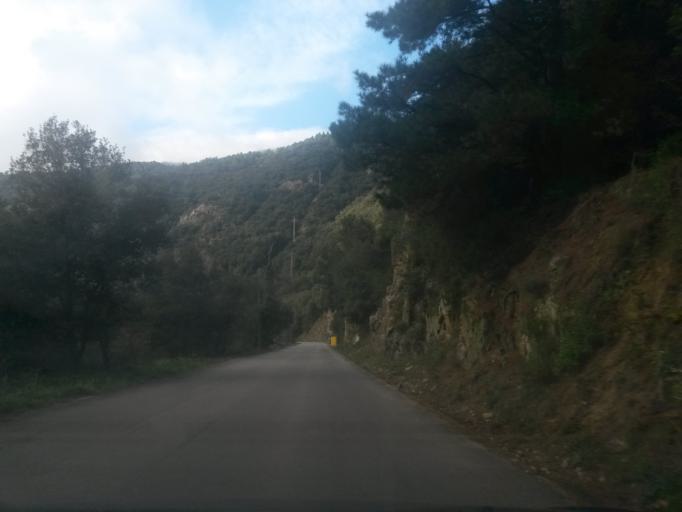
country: ES
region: Catalonia
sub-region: Provincia de Girona
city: Susqueda
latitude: 41.9853
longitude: 2.5501
